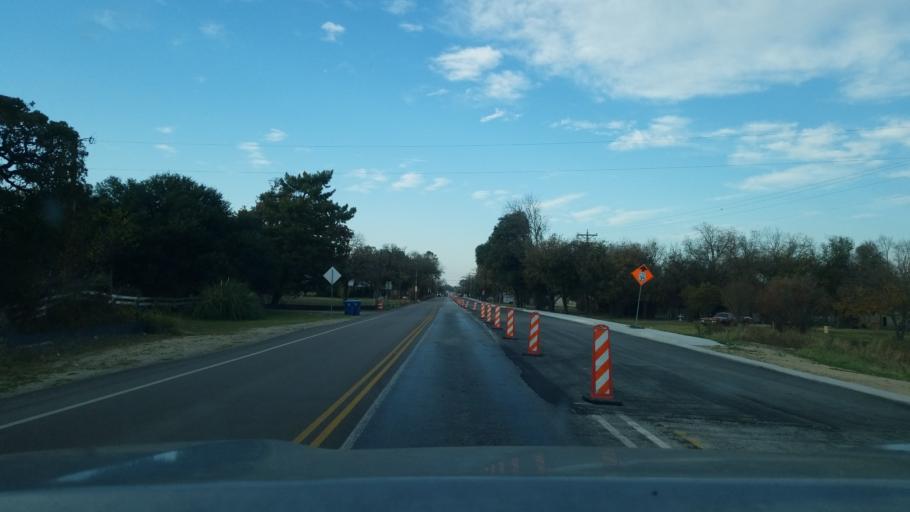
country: US
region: Texas
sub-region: Brown County
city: Lake Brownwood
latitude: 32.0865
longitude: -98.9641
